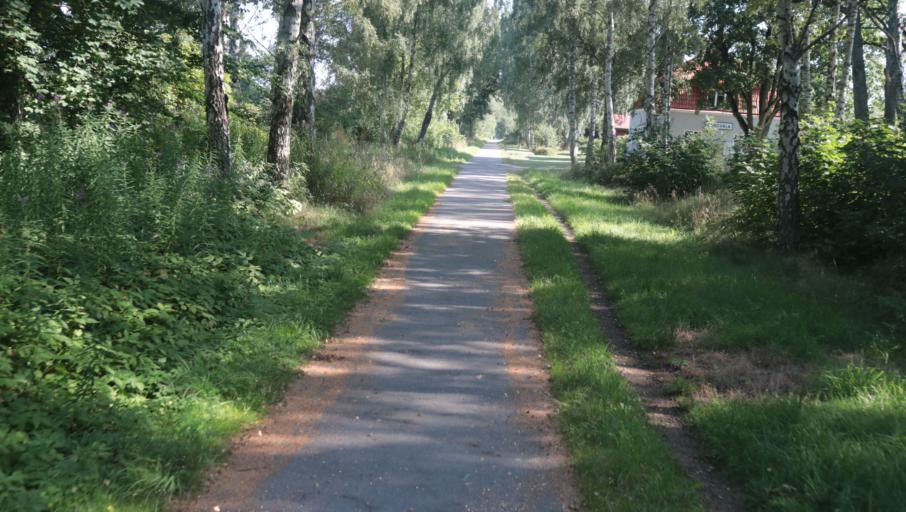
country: SE
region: Blekinge
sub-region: Karlshamns Kommun
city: Svangsta
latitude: 56.2325
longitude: 14.8096
